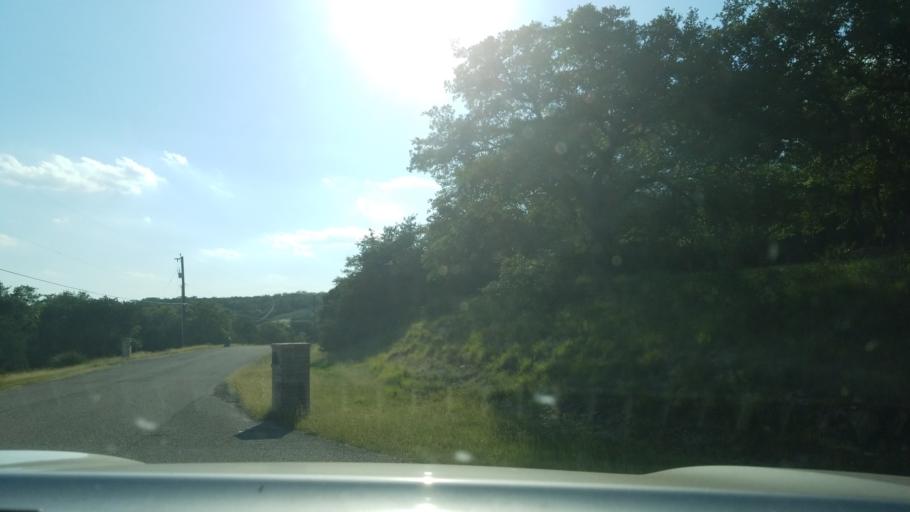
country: US
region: Texas
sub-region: Comal County
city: Bulverde
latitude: 29.7780
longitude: -98.4339
